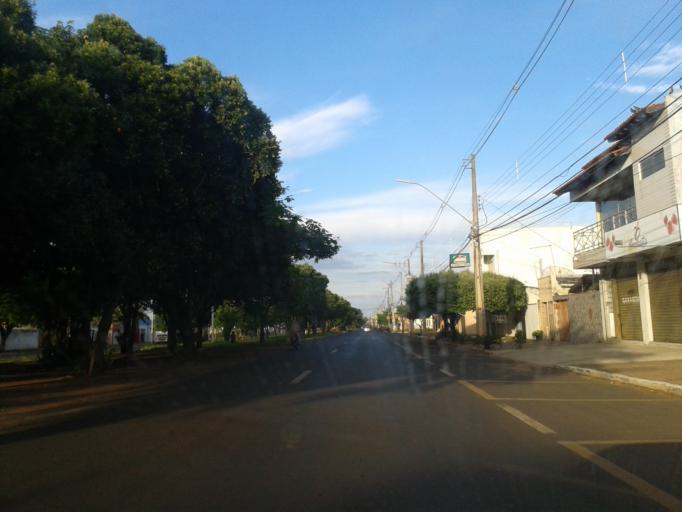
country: BR
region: Minas Gerais
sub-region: Araguari
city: Araguari
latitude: -18.6406
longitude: -48.1782
